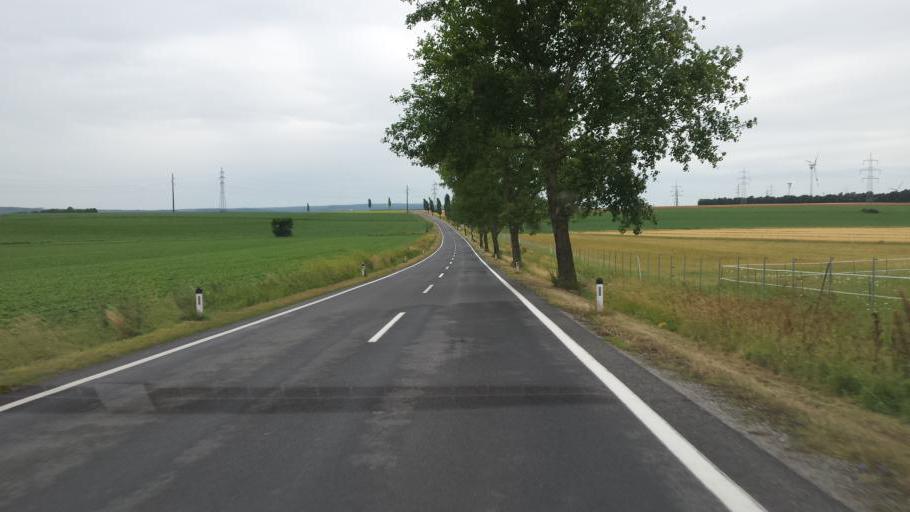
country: AT
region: Lower Austria
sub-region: Politischer Bezirk Bruck an der Leitha
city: Bruck an der Leitha
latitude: 48.0388
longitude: 16.7494
